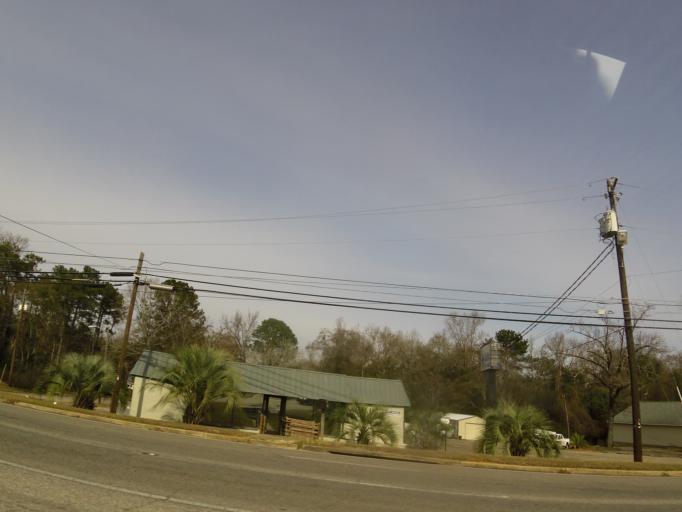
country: US
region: Alabama
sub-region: Houston County
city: Dothan
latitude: 31.2403
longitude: -85.4131
